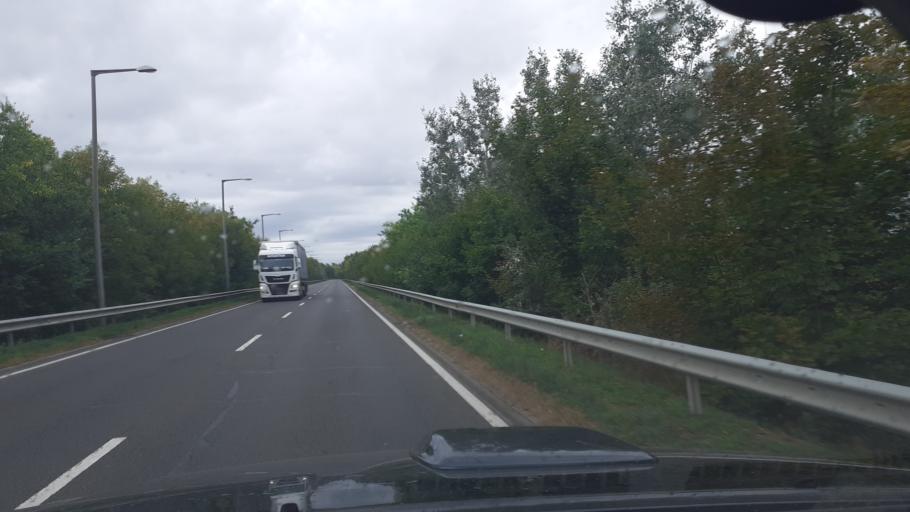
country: HU
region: Tolna
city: Dunafoldvar
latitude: 46.7990
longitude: 18.9272
